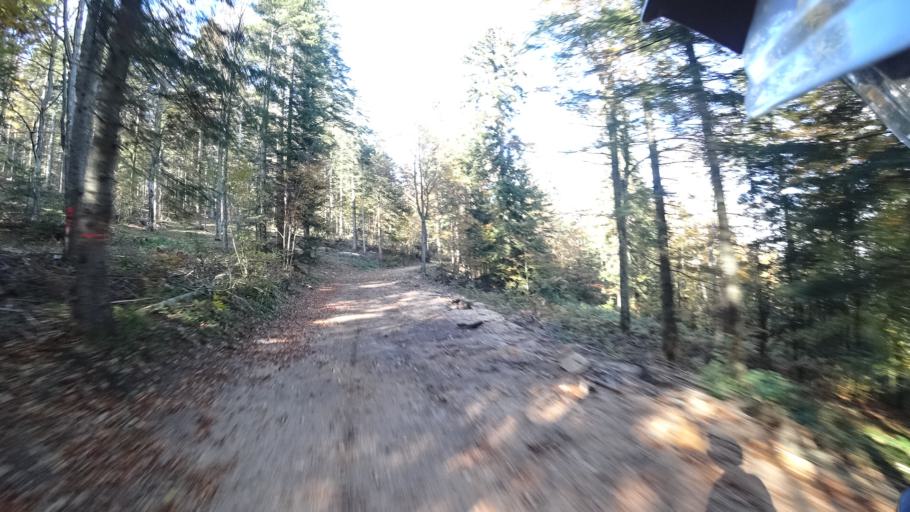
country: HR
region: Karlovacka
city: Plaski
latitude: 45.0083
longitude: 15.3891
